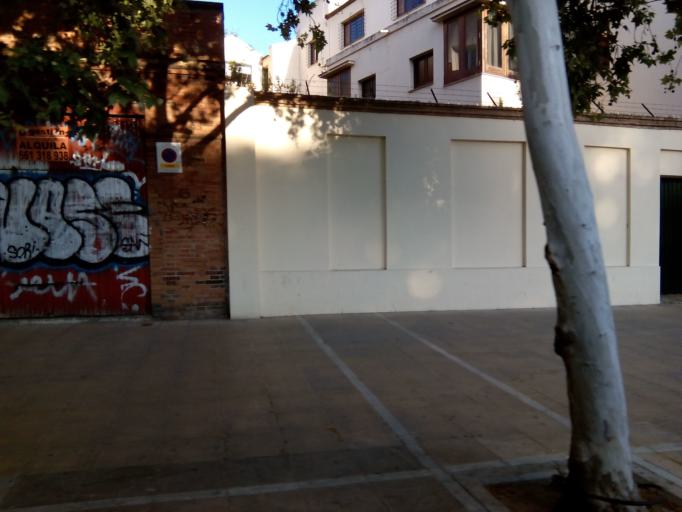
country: ES
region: Andalusia
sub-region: Provincia de Sevilla
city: Camas
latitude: 37.3960
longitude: -6.0021
